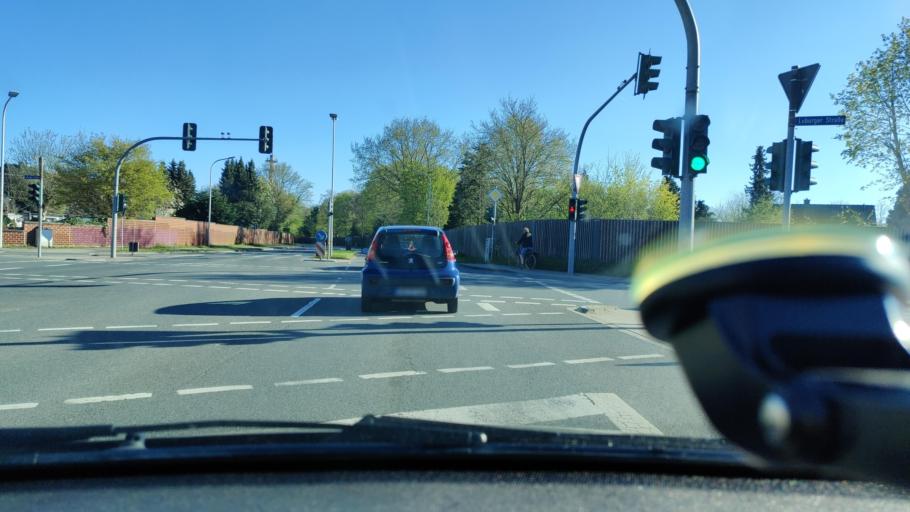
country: DE
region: North Rhine-Westphalia
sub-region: Regierungsbezirk Munster
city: Coesfeld
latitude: 51.9470
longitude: 7.1494
